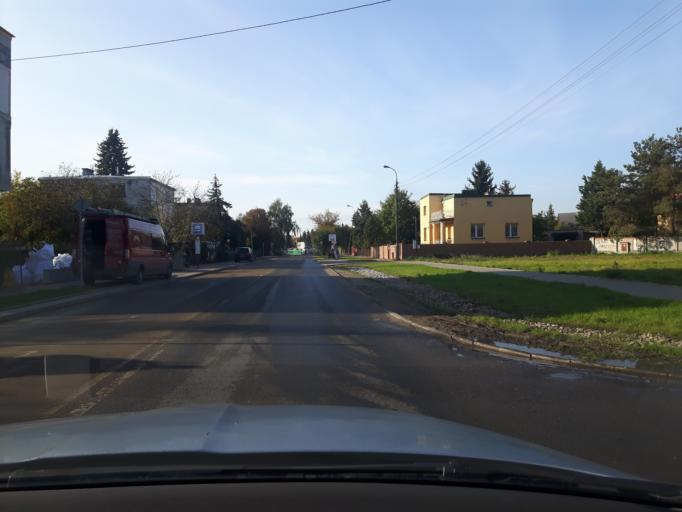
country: PL
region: Masovian Voivodeship
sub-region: Warszawa
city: Targowek
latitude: 52.2865
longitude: 21.0636
